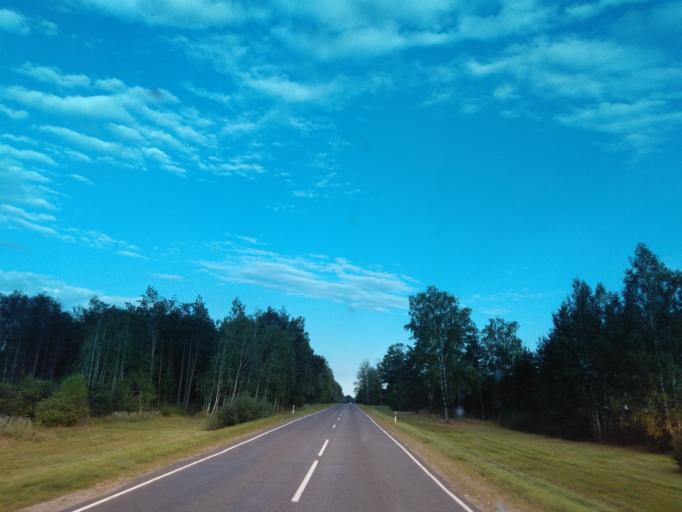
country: BY
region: Minsk
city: Uzda
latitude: 53.4316
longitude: 27.3466
